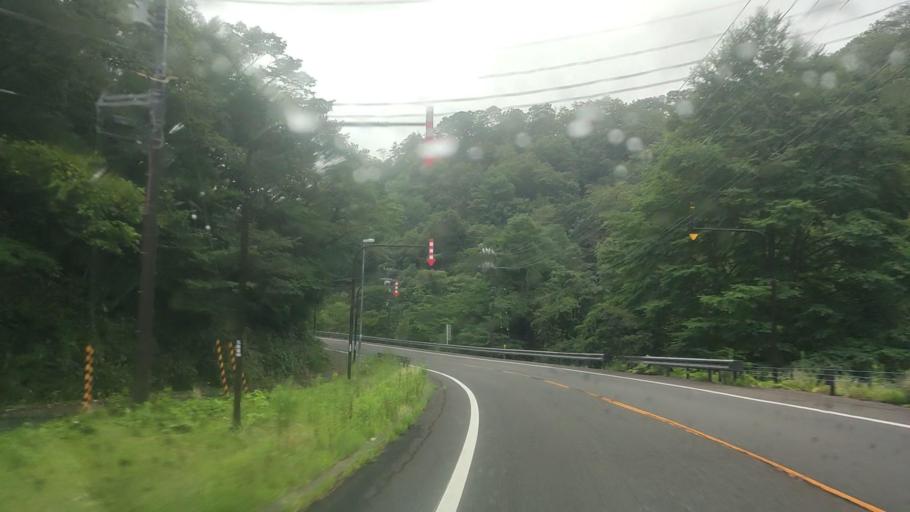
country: JP
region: Hokkaido
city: Shiraoi
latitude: 42.4854
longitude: 141.1450
